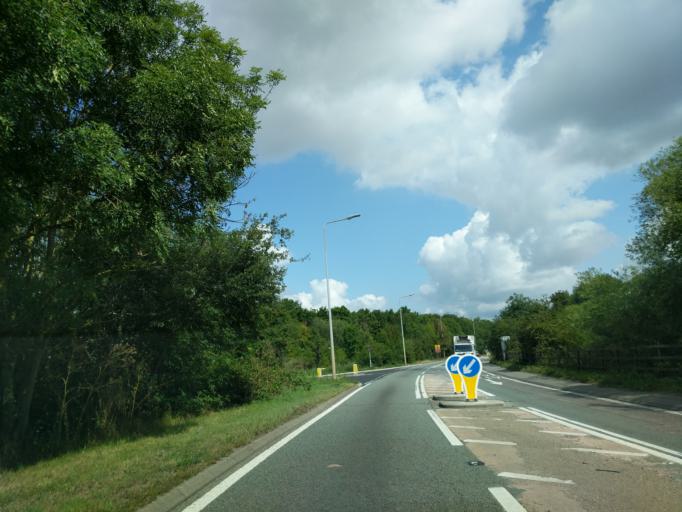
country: GB
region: England
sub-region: Suffolk
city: Exning
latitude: 52.2696
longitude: 0.3913
